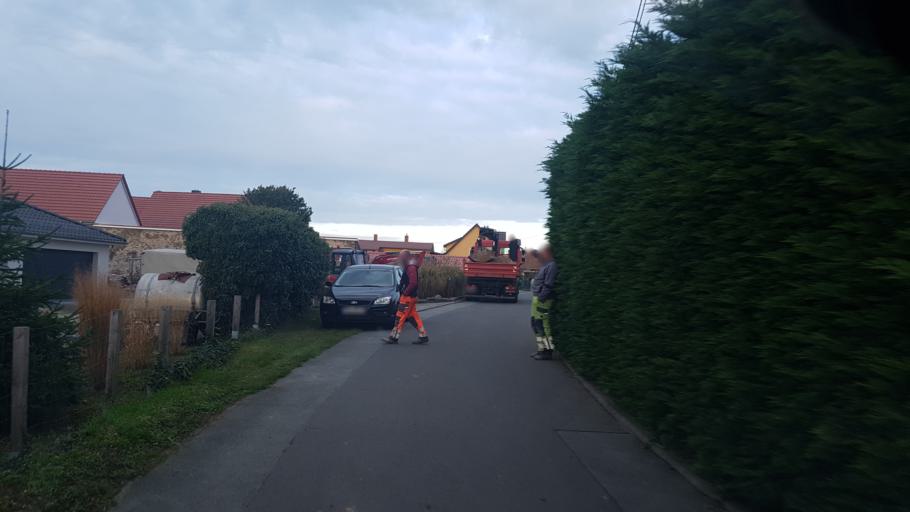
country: DE
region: Saxony
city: Cavertitz
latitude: 51.4013
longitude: 13.1279
